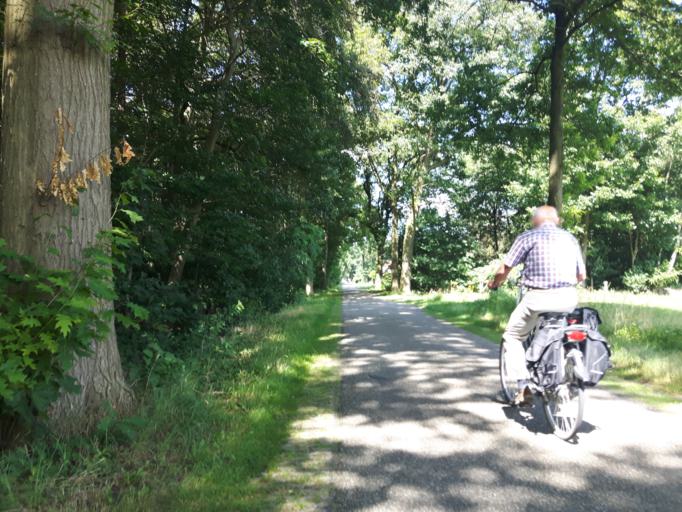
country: NL
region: Overijssel
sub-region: Gemeente Haaksbergen
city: Haaksbergen
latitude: 52.1733
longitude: 6.7594
